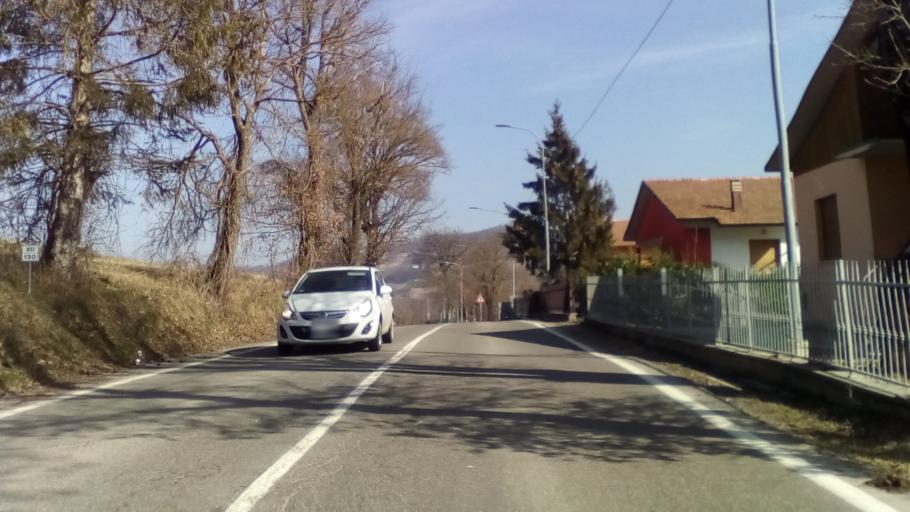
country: IT
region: Emilia-Romagna
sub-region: Provincia di Modena
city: Pavullo nel Frignano
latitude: 44.3129
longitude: 10.7958
